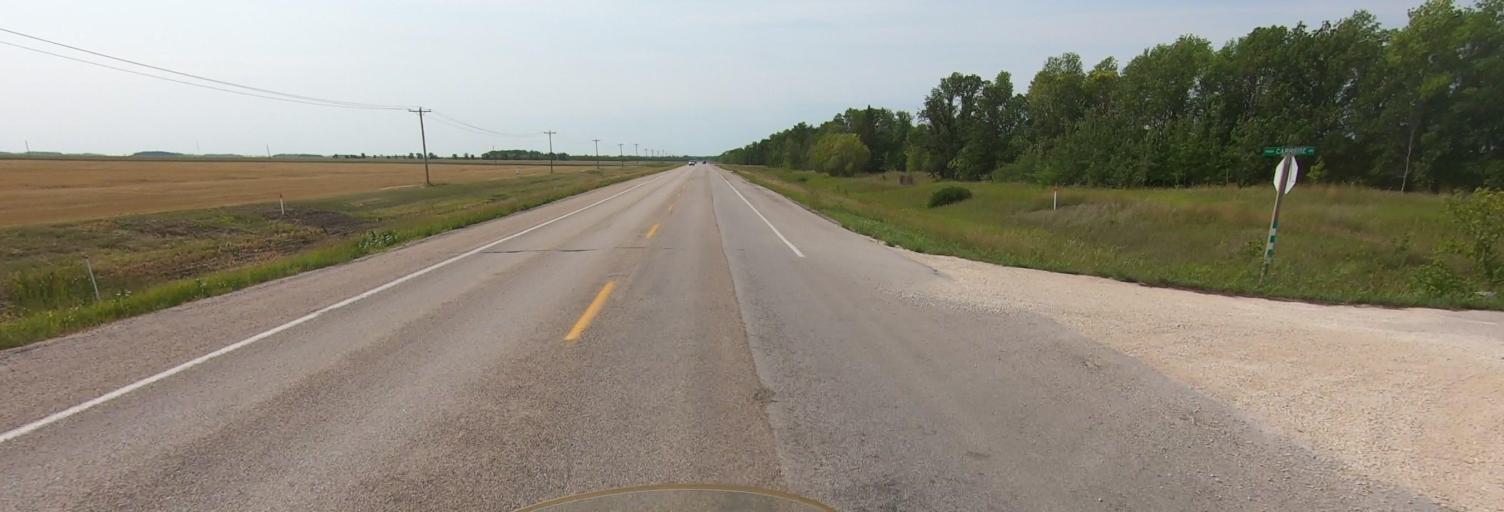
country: CA
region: Manitoba
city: Niverville
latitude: 49.6536
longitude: -97.1018
